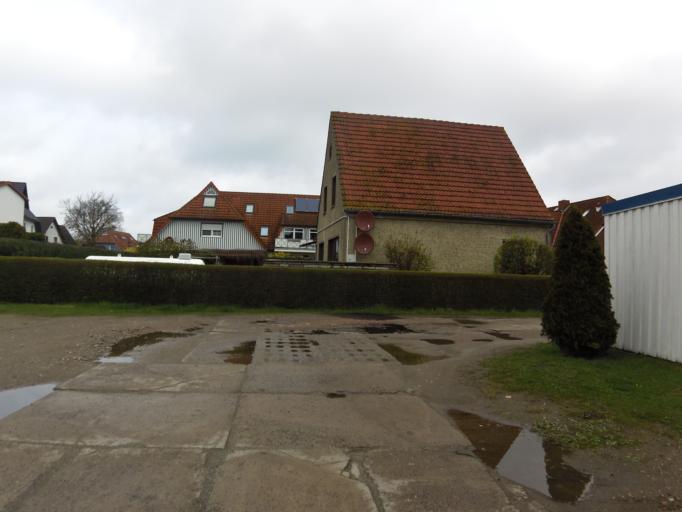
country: DE
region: Mecklenburg-Vorpommern
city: Zingst
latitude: 54.4331
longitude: 12.6910
